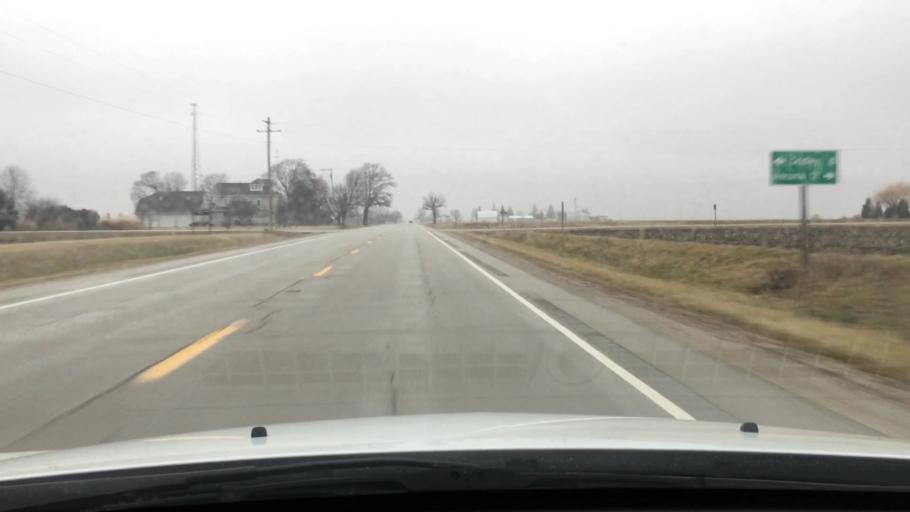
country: US
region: Illinois
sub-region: Livingston County
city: Flanagan
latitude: 40.8707
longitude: -88.8717
